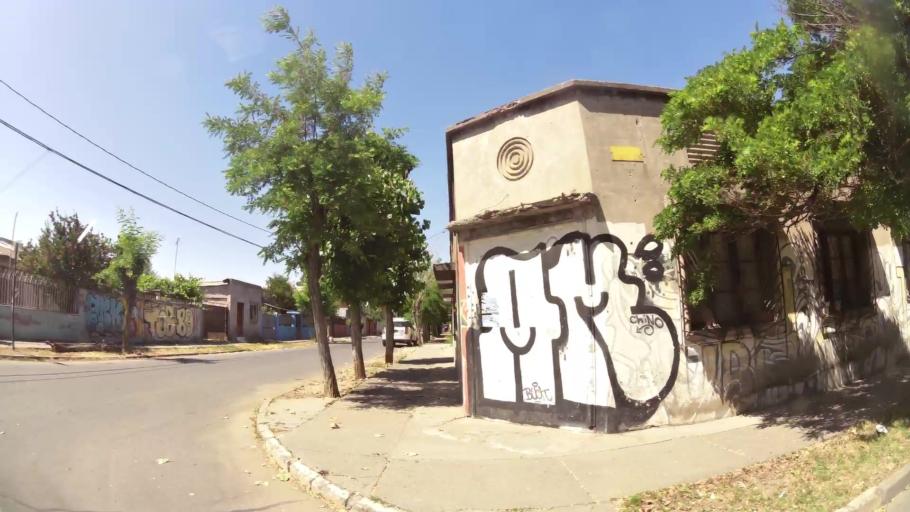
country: CL
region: Santiago Metropolitan
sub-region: Provincia de Santiago
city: La Pintana
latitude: -33.5616
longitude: -70.6685
